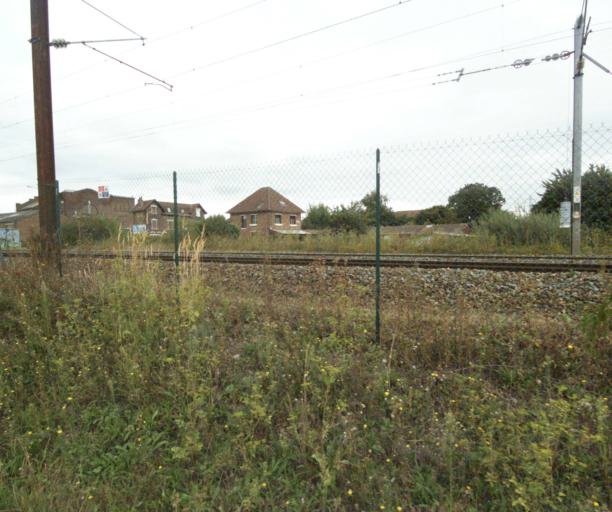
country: FR
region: Nord-Pas-de-Calais
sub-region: Departement du Nord
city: Fretin
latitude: 50.5592
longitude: 3.1503
